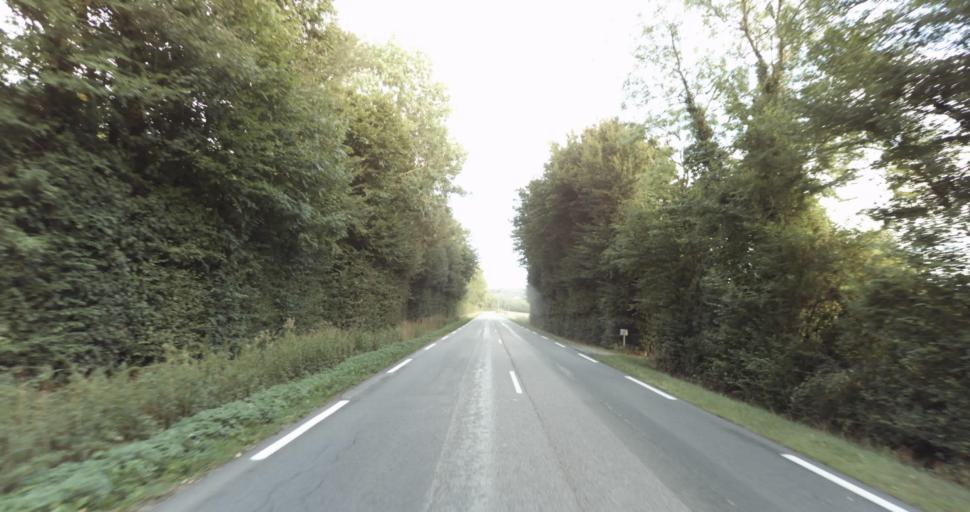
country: FR
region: Lower Normandy
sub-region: Departement de l'Orne
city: Sainte-Gauburge-Sainte-Colombe
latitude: 48.7232
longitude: 0.4207
